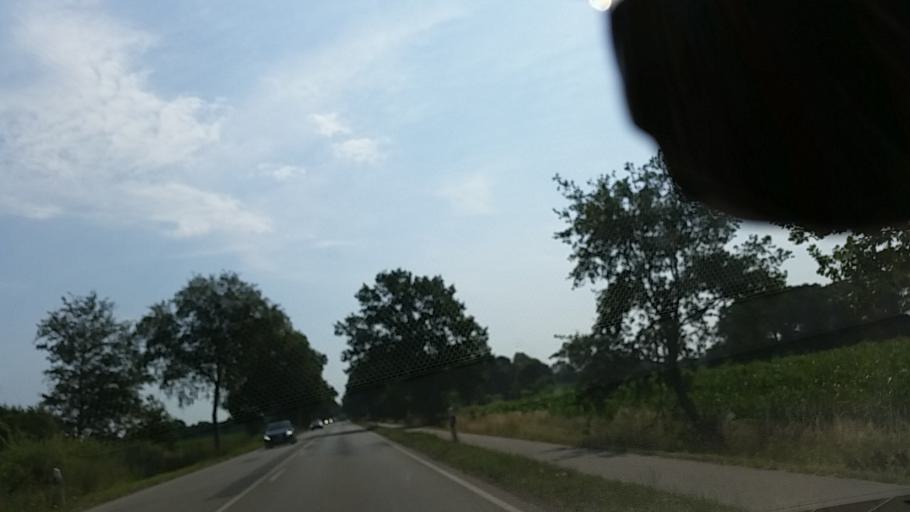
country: DE
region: Lower Saxony
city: Diepholz
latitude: 52.6106
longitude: 8.4063
